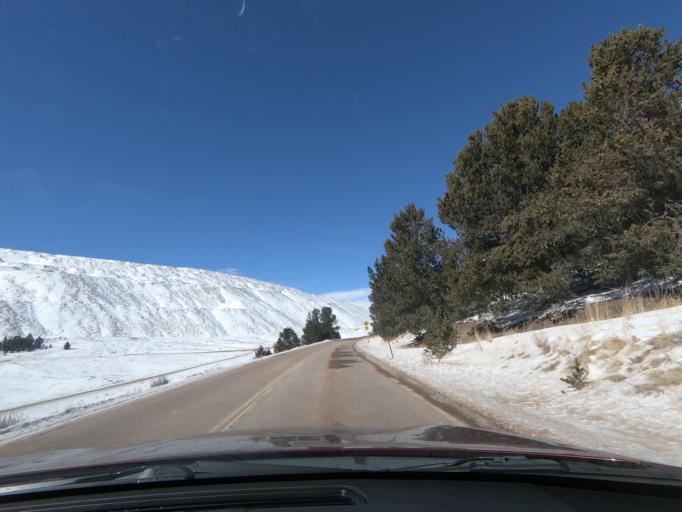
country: US
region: Colorado
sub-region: Teller County
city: Cripple Creek
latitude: 38.7413
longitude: -105.1190
